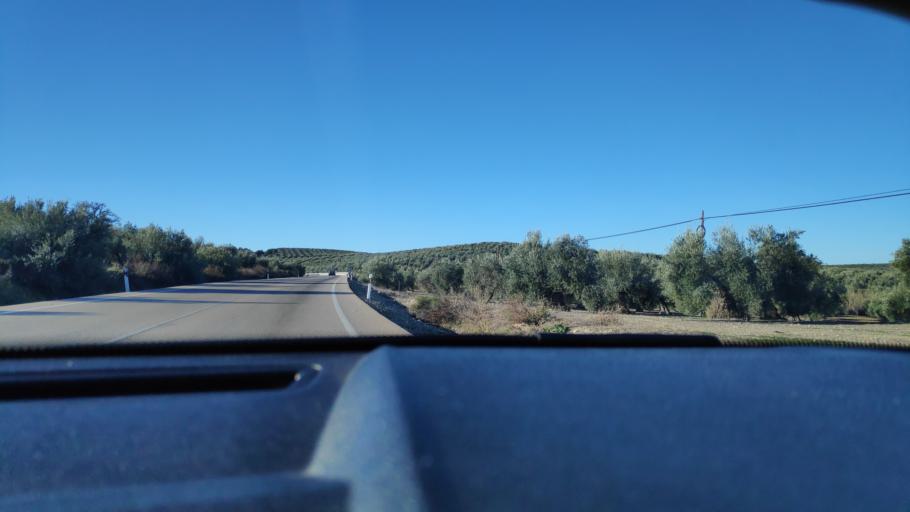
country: ES
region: Andalusia
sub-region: Provincia de Jaen
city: Mancha Real
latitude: 37.8181
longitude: -3.5765
